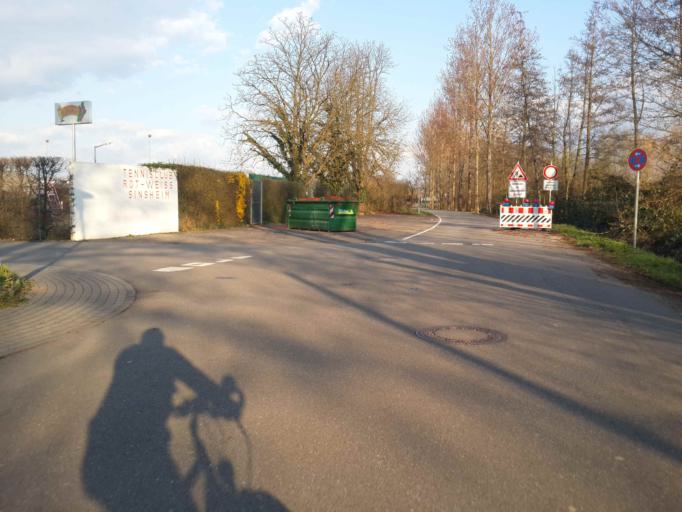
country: DE
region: Baden-Wuerttemberg
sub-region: Karlsruhe Region
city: Sinsheim
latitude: 49.2480
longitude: 8.8846
